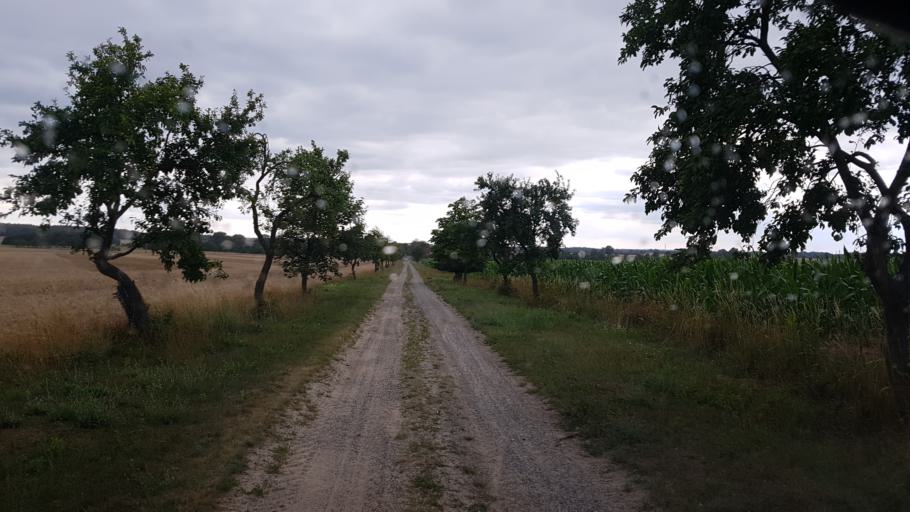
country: DE
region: Brandenburg
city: Sonnewalde
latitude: 51.7117
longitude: 13.7017
